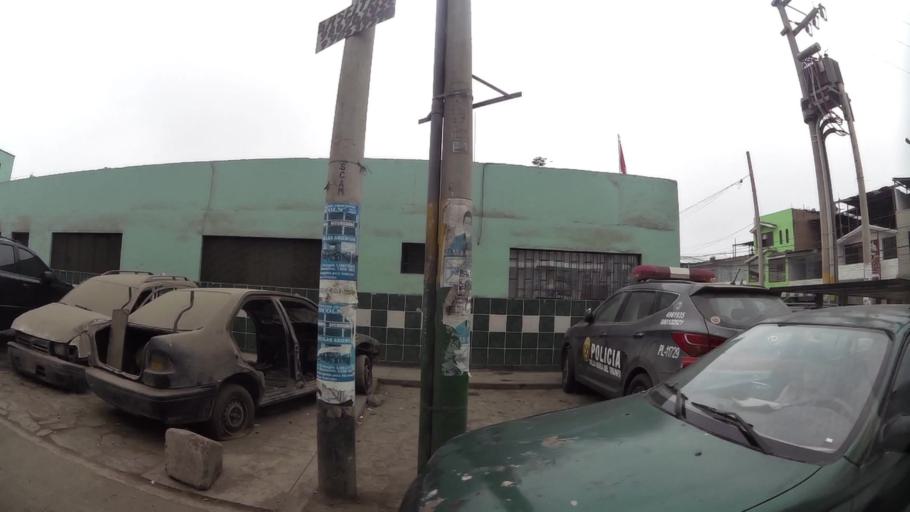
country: PE
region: Lima
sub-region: Lima
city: Surco
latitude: -12.1655
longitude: -76.9465
